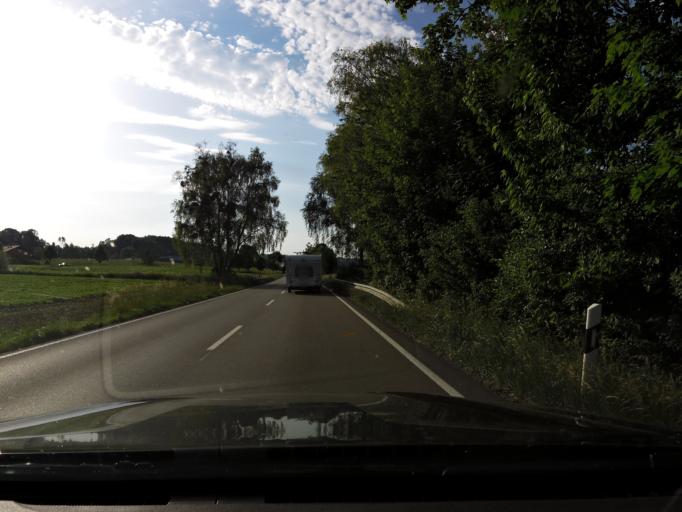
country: DE
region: Bavaria
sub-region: Upper Bavaria
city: Tittmoning
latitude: 48.0449
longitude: 12.7821
